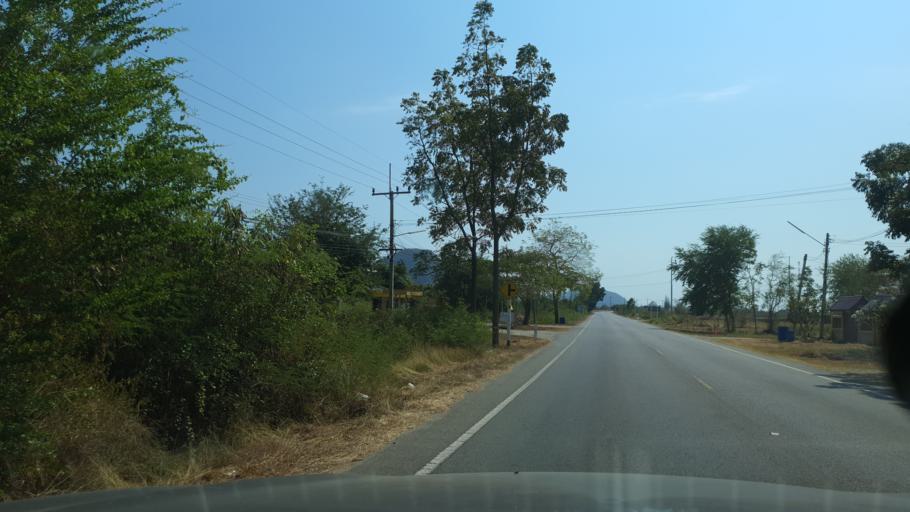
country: TH
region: Prachuap Khiri Khan
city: Sam Roi Yot
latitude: 12.2042
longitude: 99.9797
